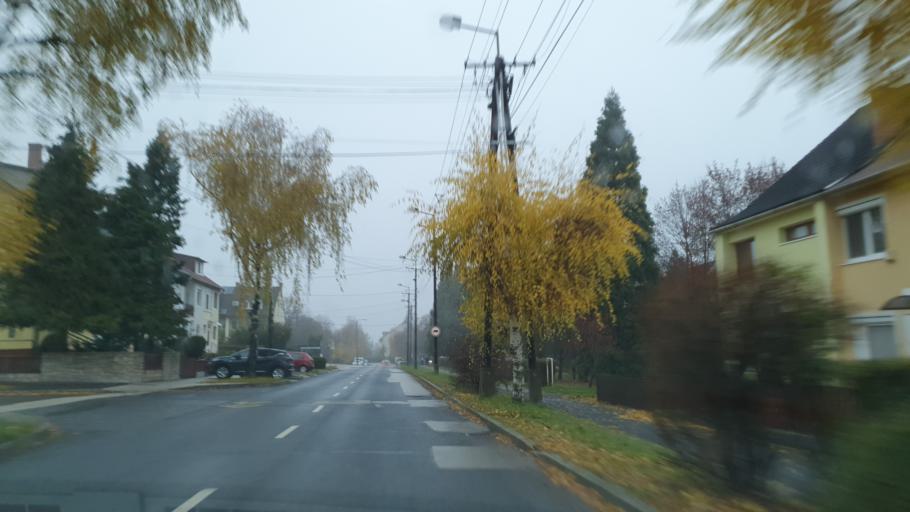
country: HU
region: Veszprem
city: Veszprem
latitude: 47.0948
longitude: 17.9293
